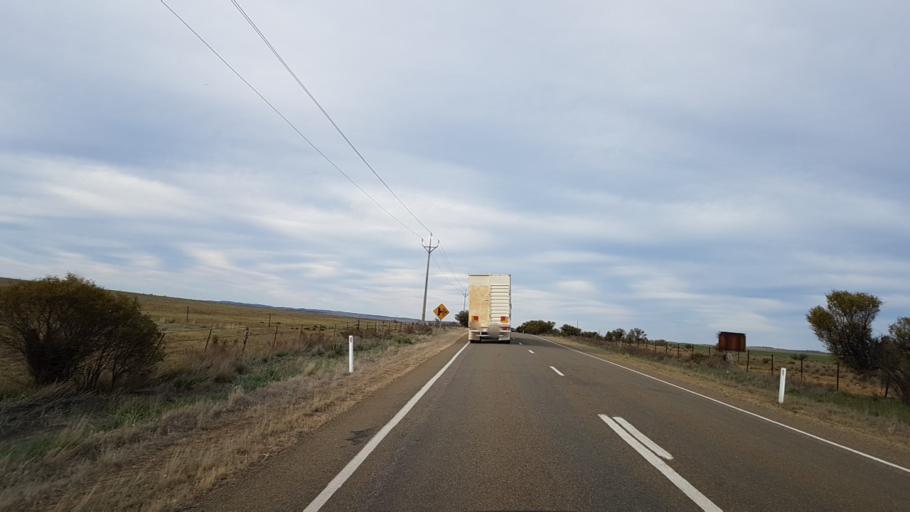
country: AU
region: South Australia
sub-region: Peterborough
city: Peterborough
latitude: -33.0178
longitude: 138.7560
